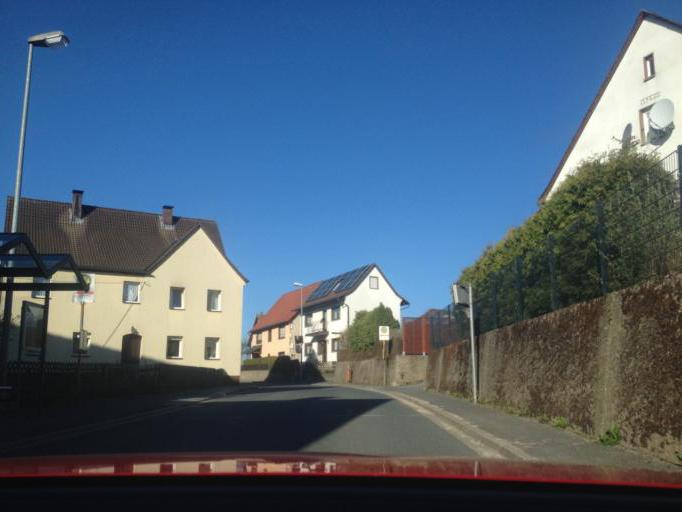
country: DE
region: Bavaria
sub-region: Regierungsbezirk Mittelfranken
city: Ruckersdorf
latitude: 49.5326
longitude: 11.2194
